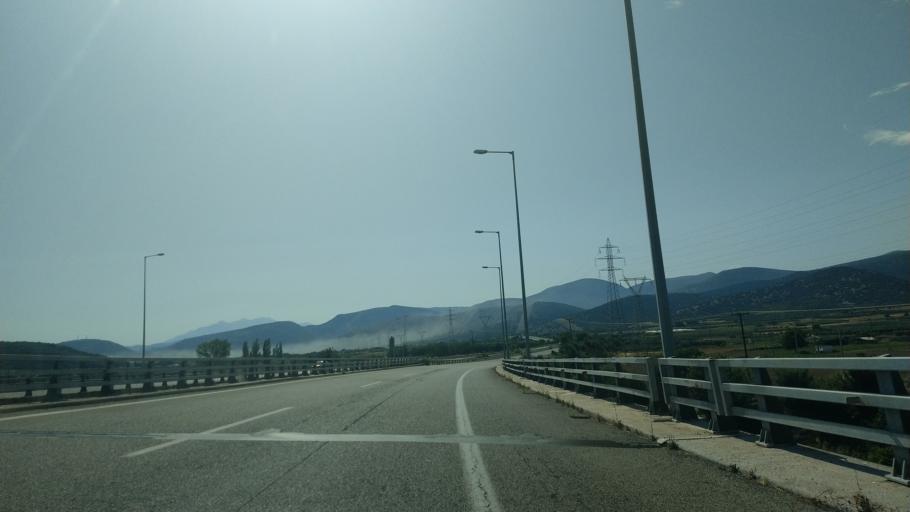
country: GR
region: East Macedonia and Thrace
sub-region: Nomos Kavalas
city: Nea Karvali
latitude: 40.9671
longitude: 24.5215
